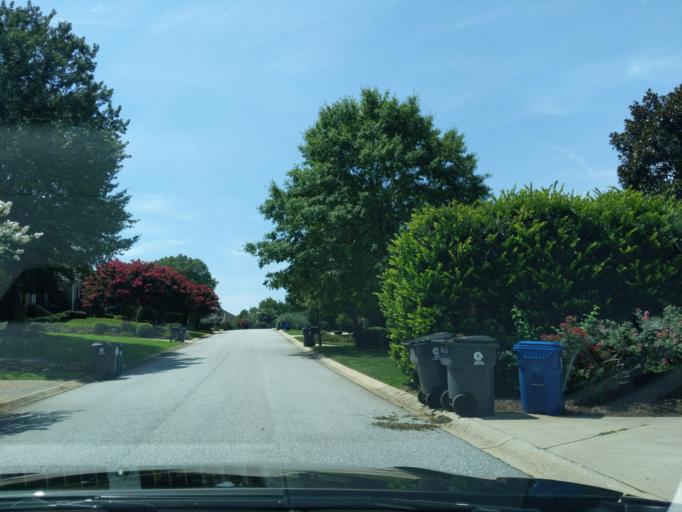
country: US
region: South Carolina
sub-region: Greenville County
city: Five Forks
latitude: 34.8363
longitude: -82.2155
